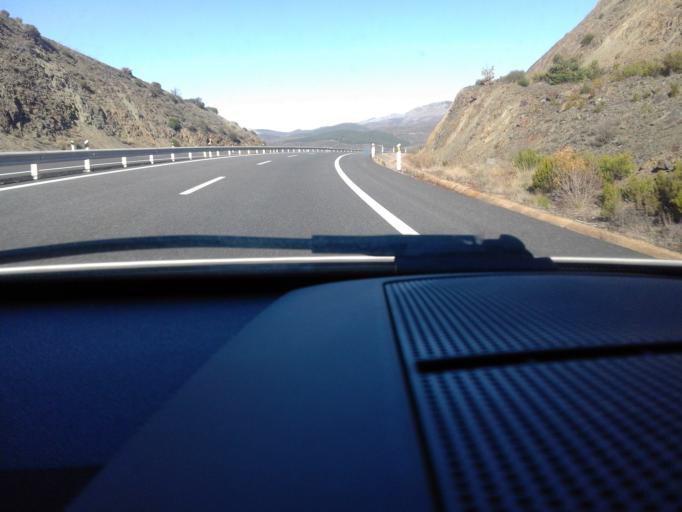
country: ES
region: Castille and Leon
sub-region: Provincia de Leon
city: Carrocera
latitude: 42.7532
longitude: -5.7725
